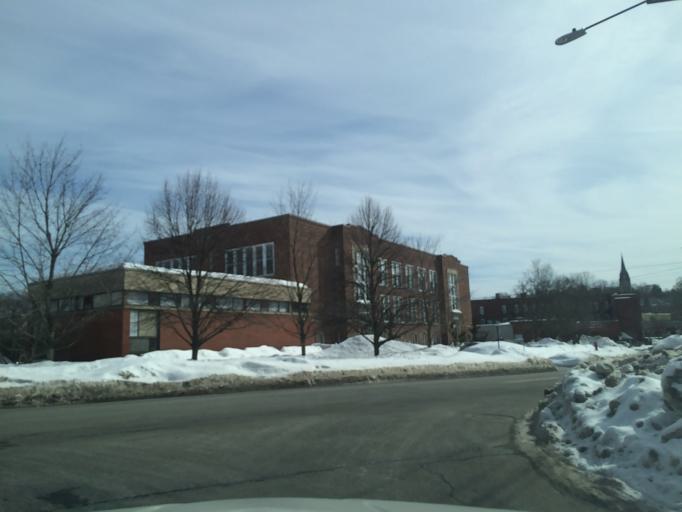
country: US
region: Massachusetts
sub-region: Middlesex County
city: Newton
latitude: 42.3513
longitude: -71.2266
